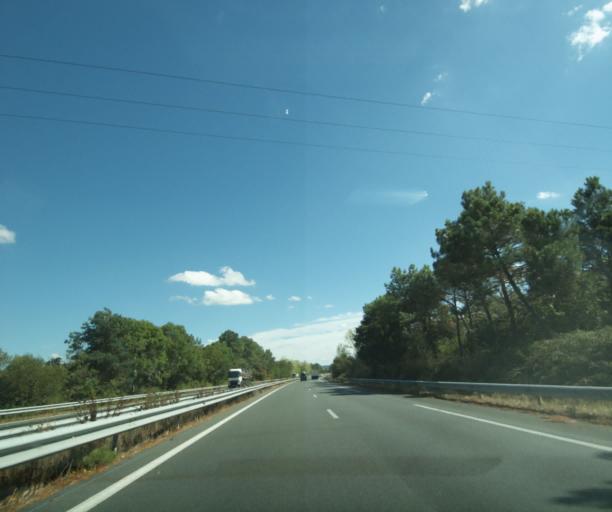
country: FR
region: Aquitaine
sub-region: Departement du Lot-et-Garonne
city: Tonneins
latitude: 44.3765
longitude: 0.2276
